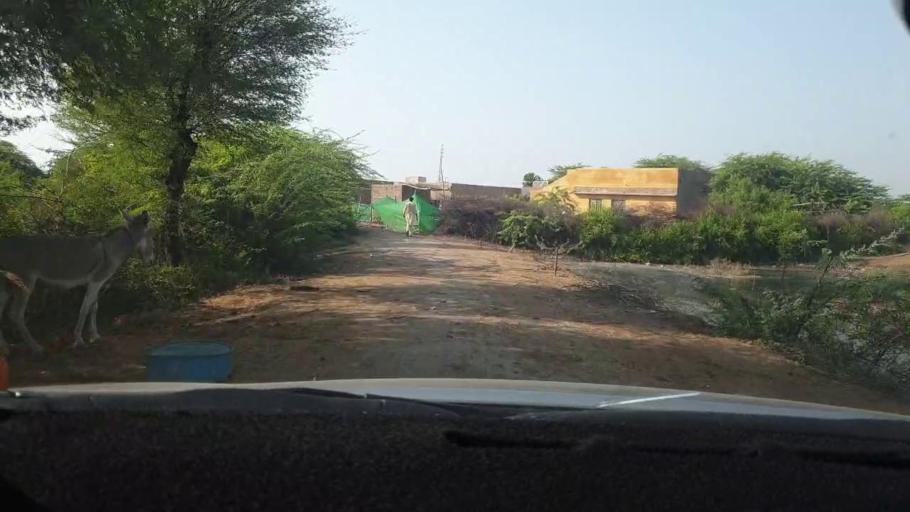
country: PK
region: Sindh
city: Pithoro
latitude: 25.7940
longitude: 69.4123
